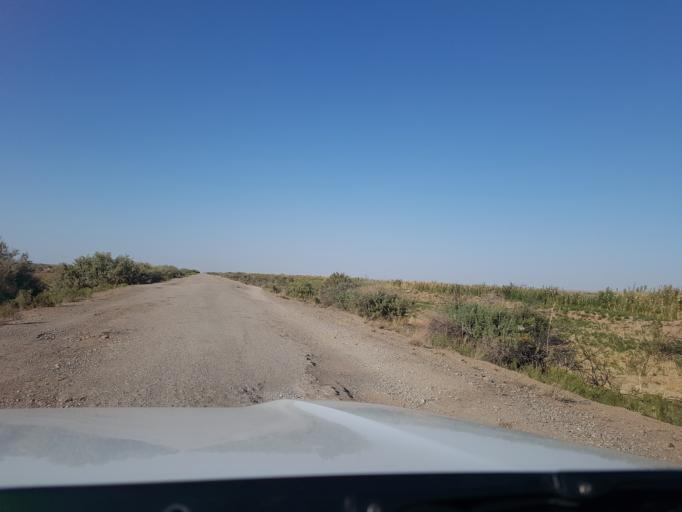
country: IR
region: Razavi Khorasan
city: Sarakhs
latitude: 36.9518
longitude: 61.3802
